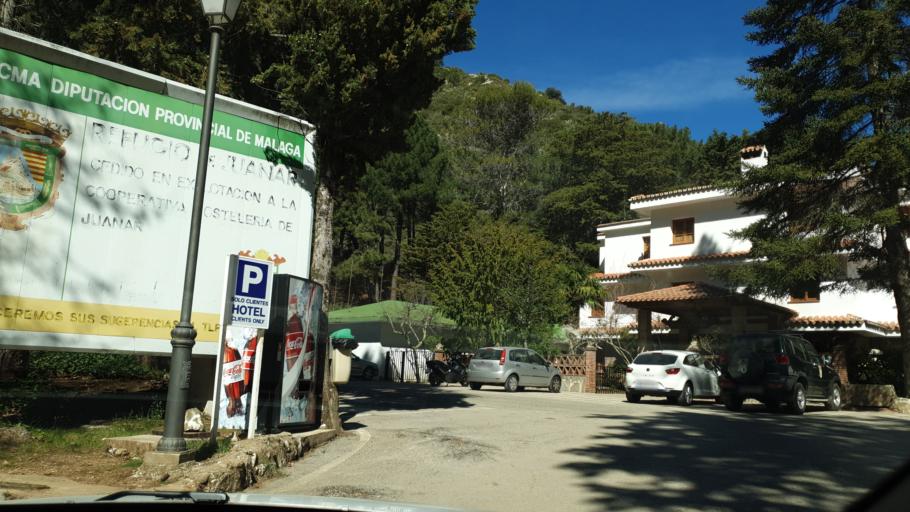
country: ES
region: Andalusia
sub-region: Provincia de Malaga
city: Ojen
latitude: 36.5796
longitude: -4.8852
